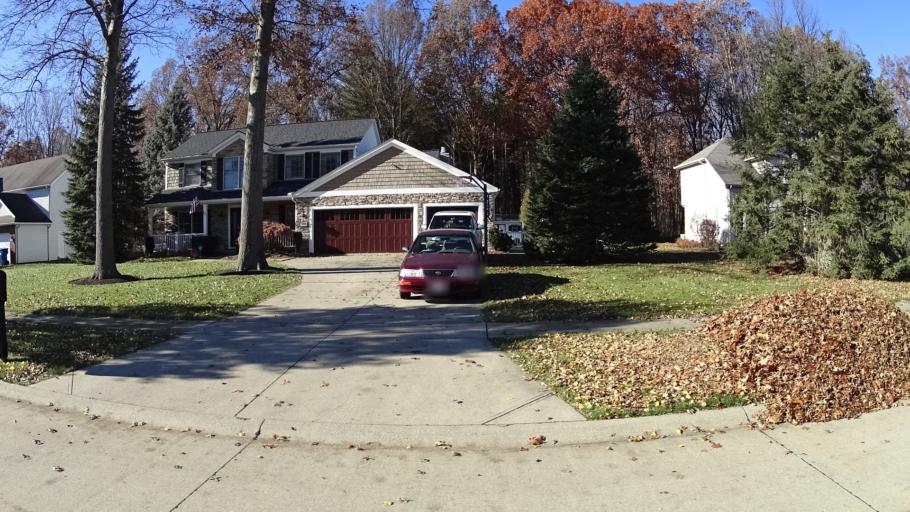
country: US
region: Ohio
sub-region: Lorain County
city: Avon Center
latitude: 41.4378
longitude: -82.0081
